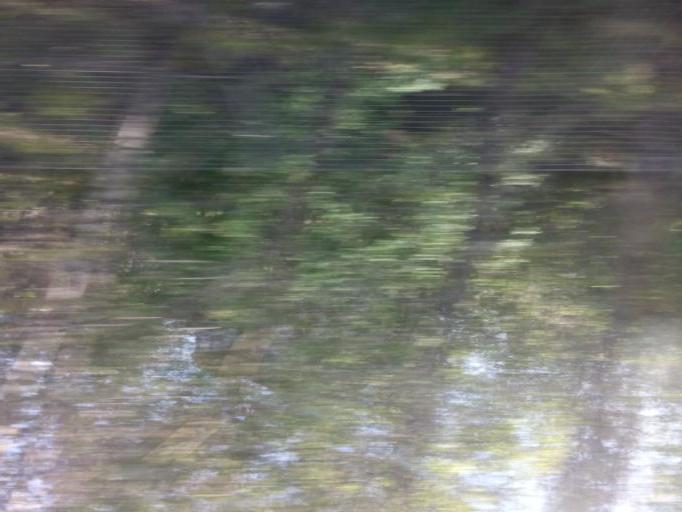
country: GB
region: Scotland
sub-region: Edinburgh
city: Currie
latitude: 55.9371
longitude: -3.3024
